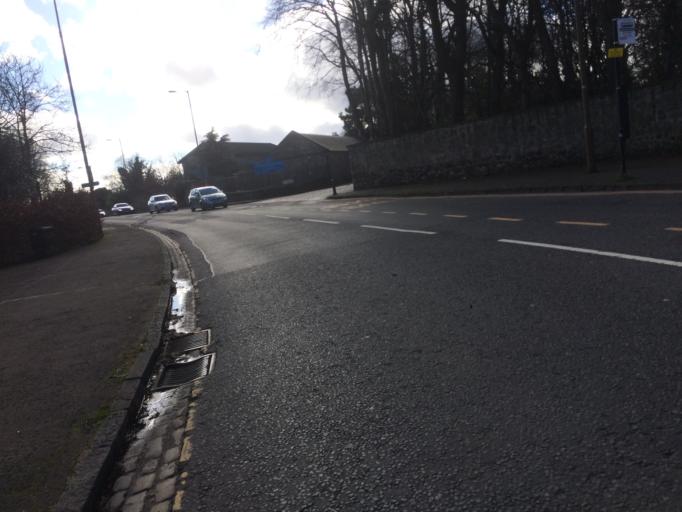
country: GB
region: Scotland
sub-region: West Lothian
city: Seafield
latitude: 55.9422
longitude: -3.1448
